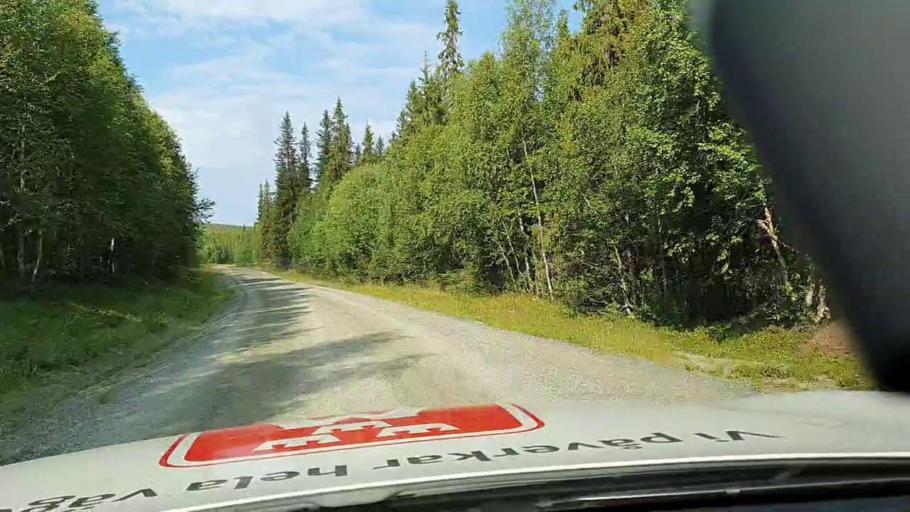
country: SE
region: Vaesterbotten
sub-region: Storumans Kommun
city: Fristad
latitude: 65.5382
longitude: 16.8072
